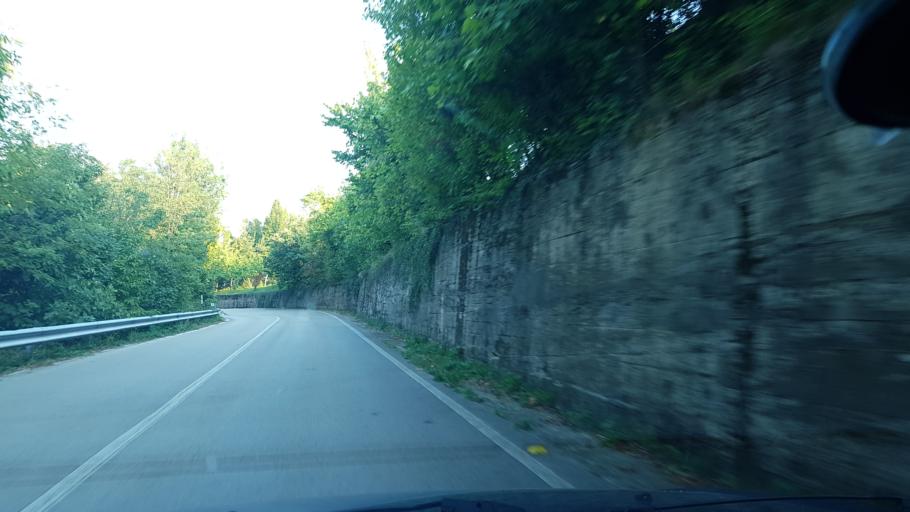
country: IT
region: Friuli Venezia Giulia
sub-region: Provincia di Gorizia
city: San Floriano del Collio
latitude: 45.9847
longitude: 13.5919
